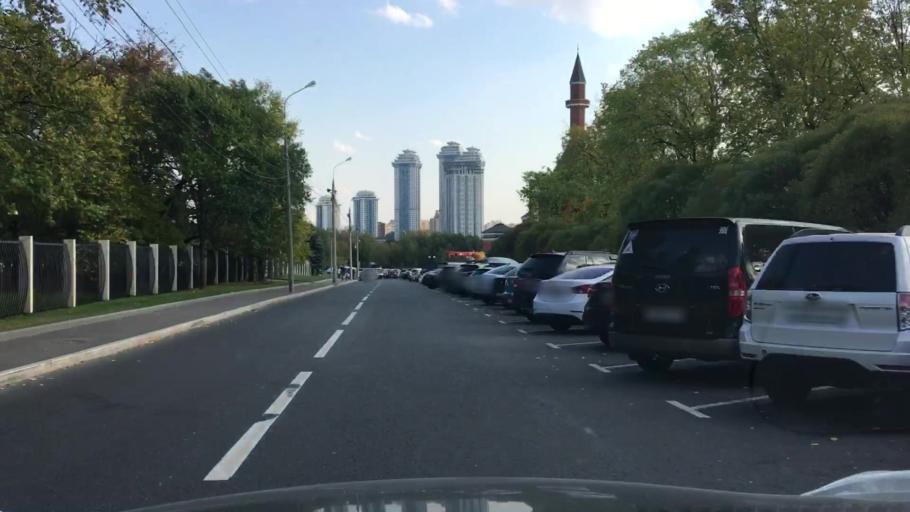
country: RU
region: Moskovskaya
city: Kastanayevo
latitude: 55.7271
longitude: 37.4963
